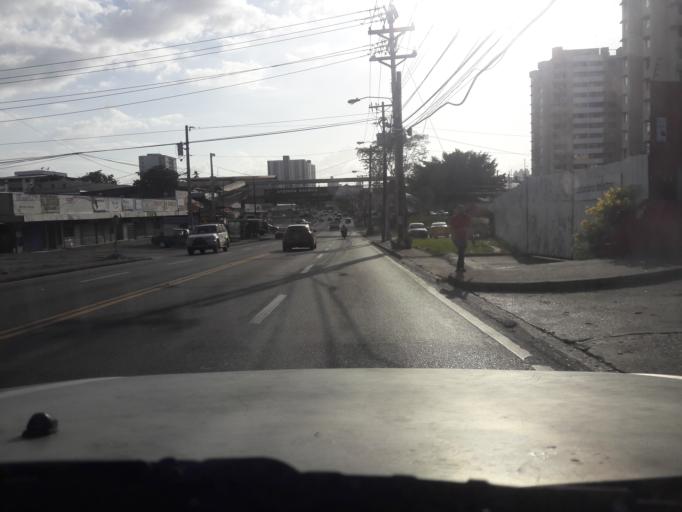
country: PA
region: Panama
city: San Miguelito
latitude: 9.0222
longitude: -79.4892
